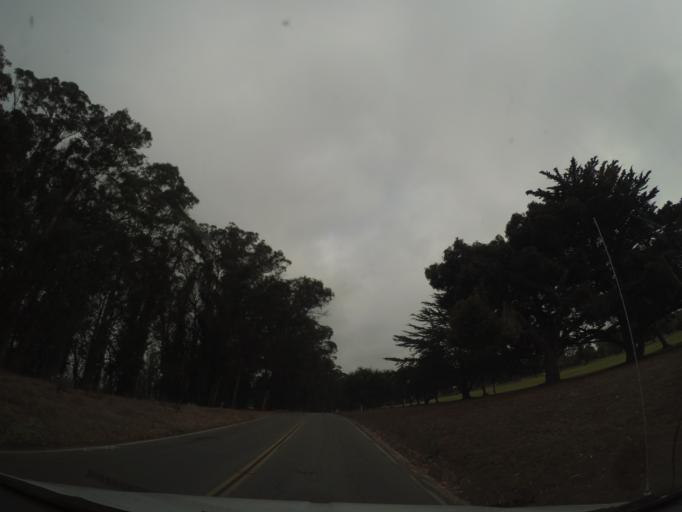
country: US
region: California
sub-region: San Luis Obispo County
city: Morro Bay
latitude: 35.3510
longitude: -120.8432
